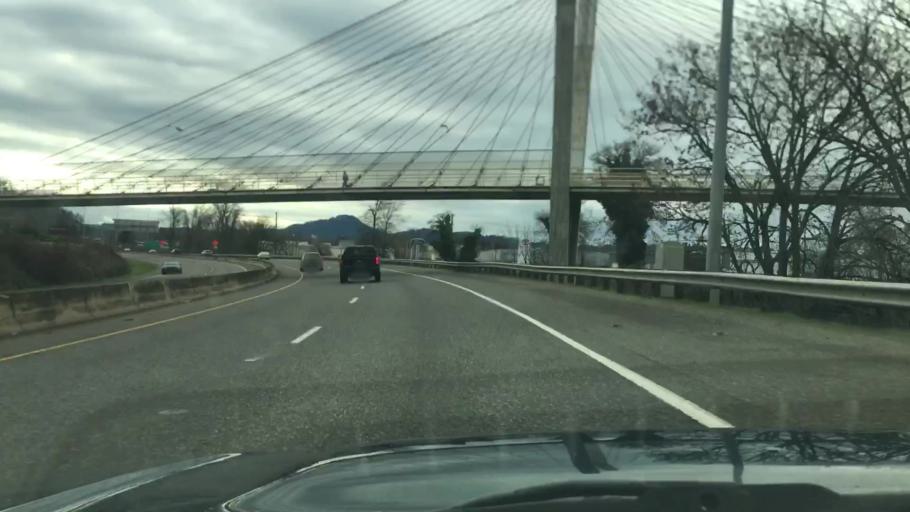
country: US
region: Oregon
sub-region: Lane County
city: Eugene
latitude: 44.0766
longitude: -123.1057
